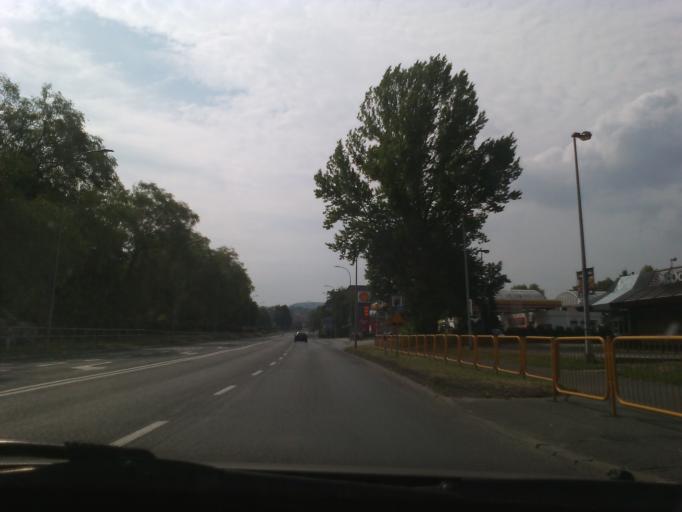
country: PL
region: Lower Silesian Voivodeship
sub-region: Powiat walbrzyski
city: Walbrzych
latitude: 50.7750
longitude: 16.2742
